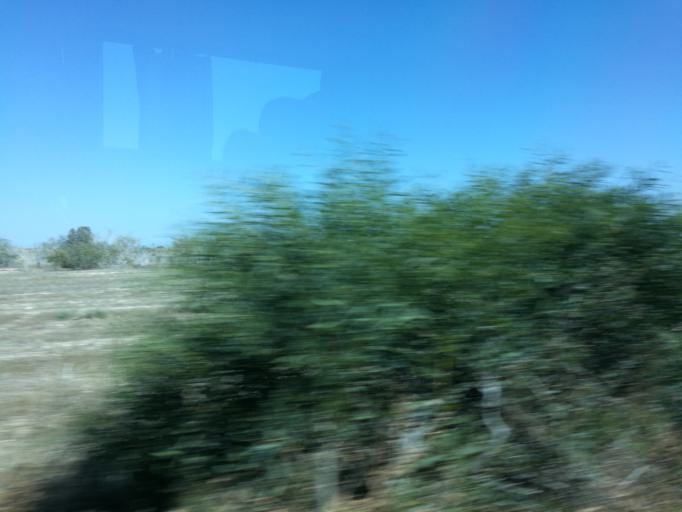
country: CY
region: Ammochostos
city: Acheritou
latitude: 35.0754
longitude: 33.8650
